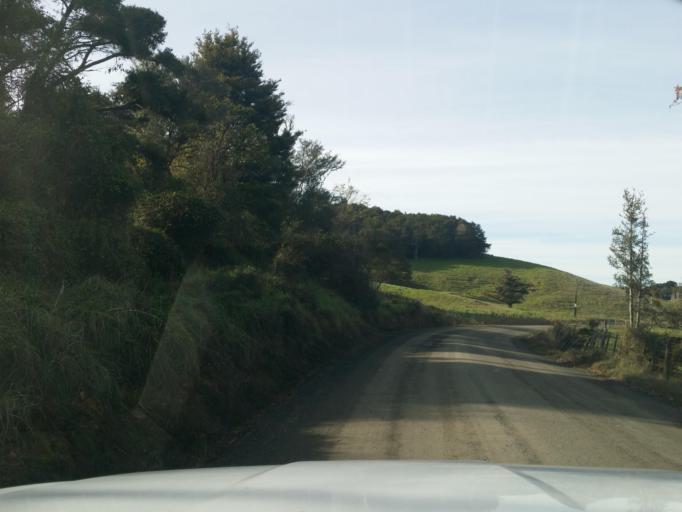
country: NZ
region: Northland
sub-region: Kaipara District
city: Dargaville
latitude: -35.8172
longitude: 173.9061
